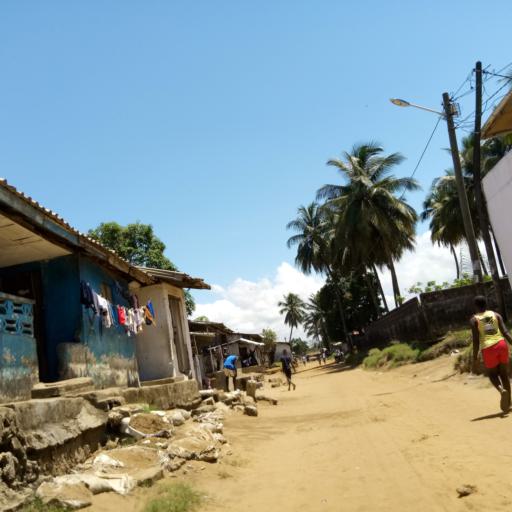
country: LR
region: Montserrado
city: Monrovia
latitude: 6.2396
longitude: -10.6948
